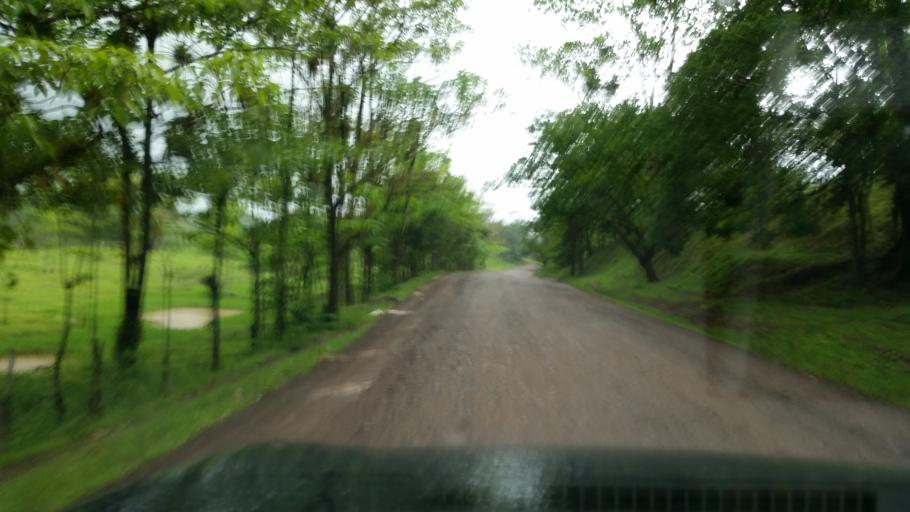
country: NI
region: Atlantico Norte (RAAN)
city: Siuna
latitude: 13.4027
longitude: -84.8539
